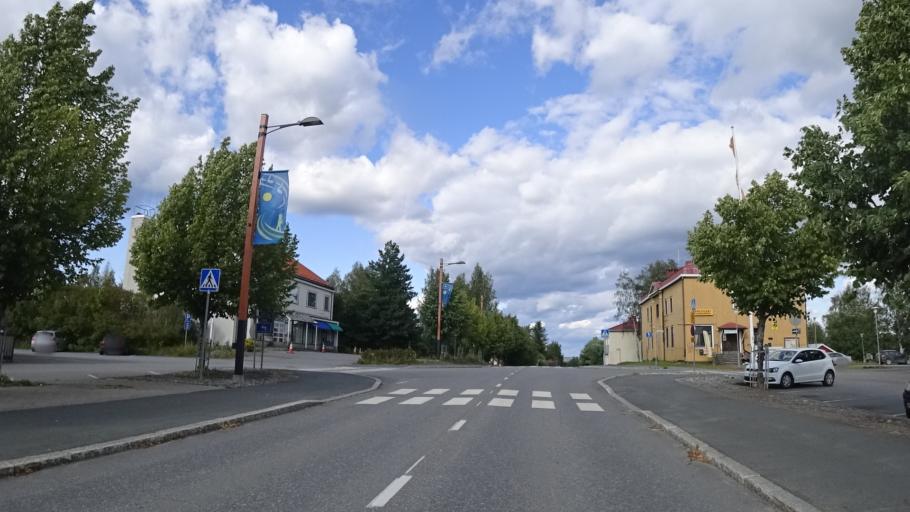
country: FI
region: North Karelia
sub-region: Keski-Karjala
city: Tohmajaervi
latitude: 62.2248
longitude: 30.3304
